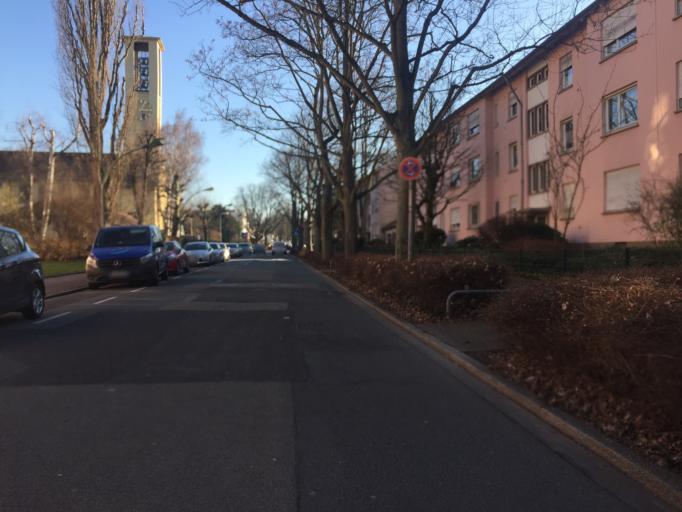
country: DE
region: Hesse
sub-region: Regierungsbezirk Darmstadt
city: Frankfurt am Main
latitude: 50.1518
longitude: 8.6693
